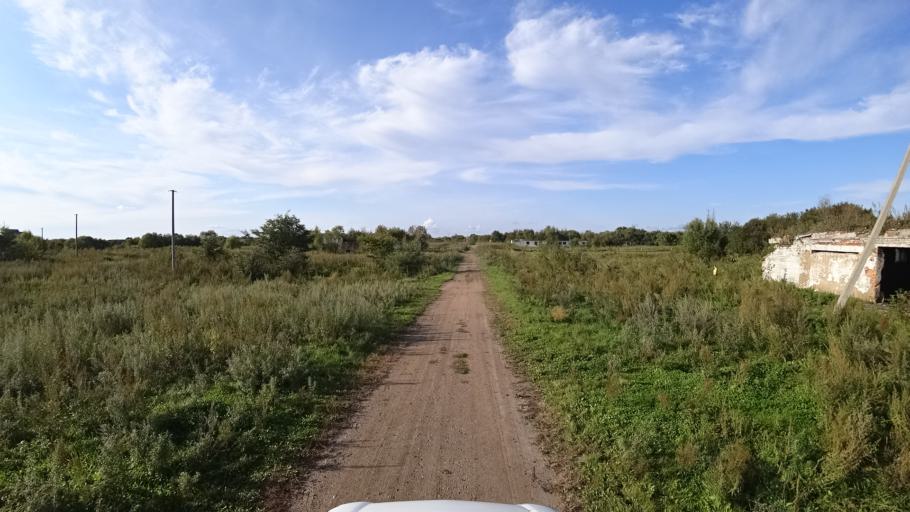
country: RU
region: Amur
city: Arkhara
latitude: 49.3474
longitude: 130.1070
